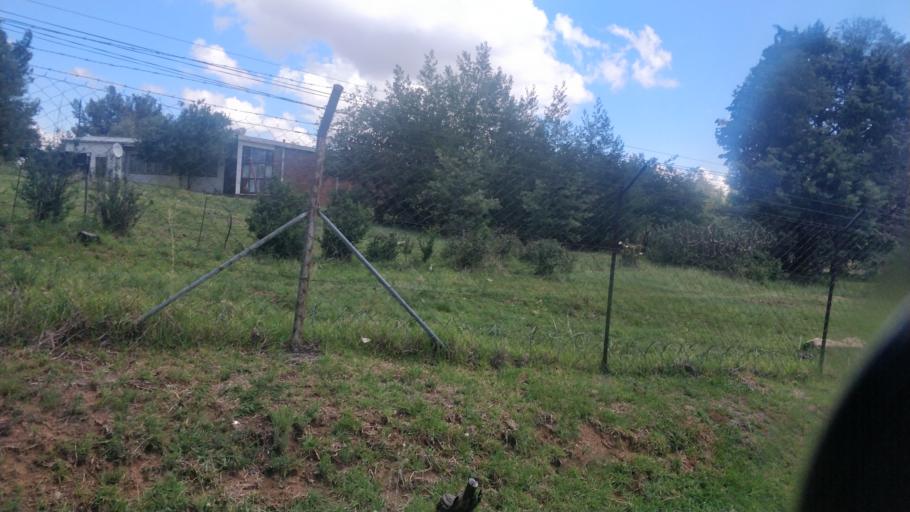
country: LS
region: Maseru
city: Nako
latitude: -29.6298
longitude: 27.5020
